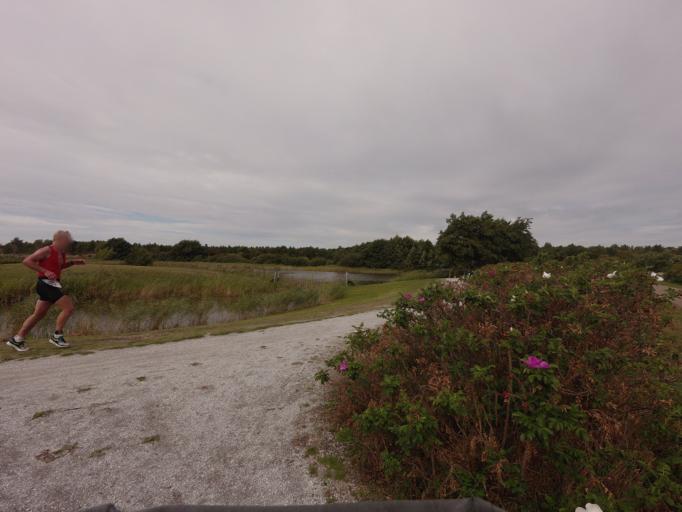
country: NL
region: Friesland
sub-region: Gemeente Ameland
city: Nes
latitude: 53.4510
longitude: 5.7814
